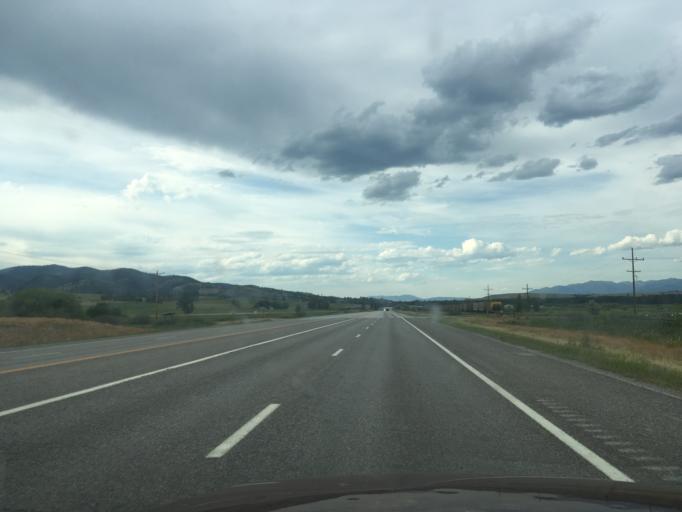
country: US
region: Montana
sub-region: Missoula County
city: Lolo
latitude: 46.7264
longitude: -114.0786
